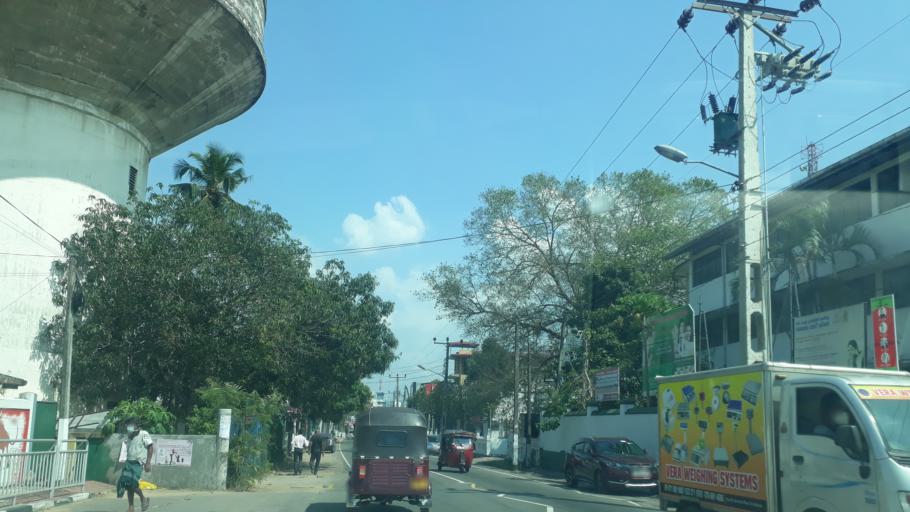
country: LK
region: Western
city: Gampaha
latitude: 7.0904
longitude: 80.0020
